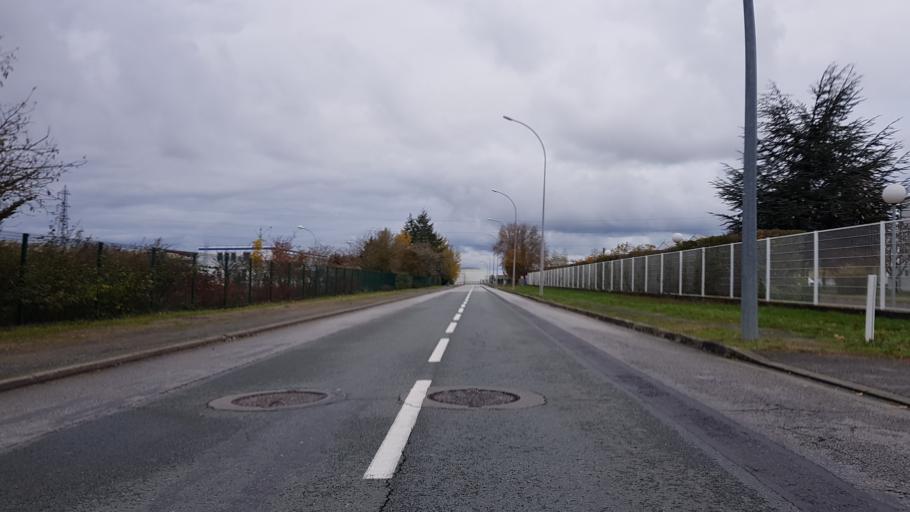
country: FR
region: Poitou-Charentes
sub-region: Departement de la Vienne
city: Chasseneuil-du-Poitou
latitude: 46.6597
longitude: 0.3720
